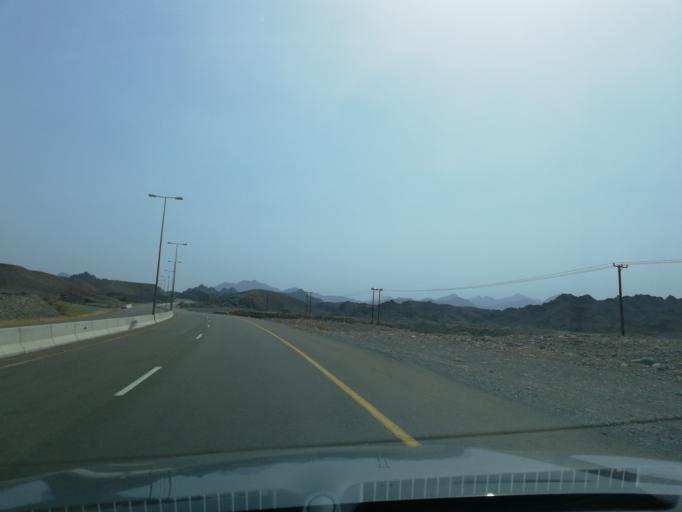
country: OM
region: Al Batinah
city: Al Liwa'
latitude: 24.2814
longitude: 56.4053
